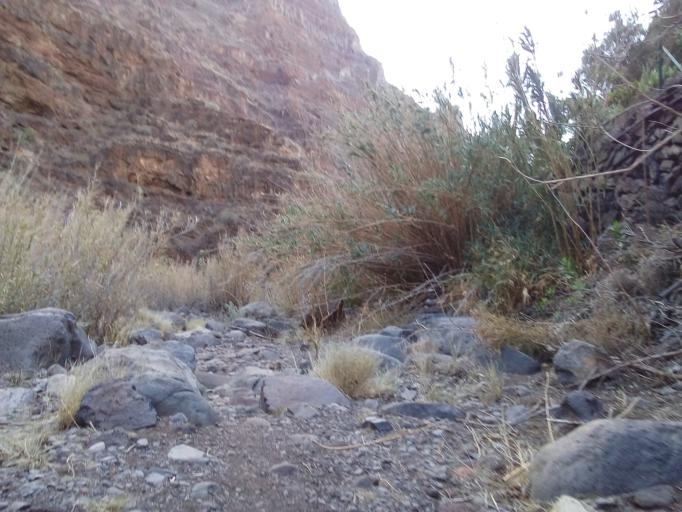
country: ES
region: Canary Islands
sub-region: Provincia de Santa Cruz de Tenerife
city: Alajero
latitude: 28.0826
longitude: -17.3213
